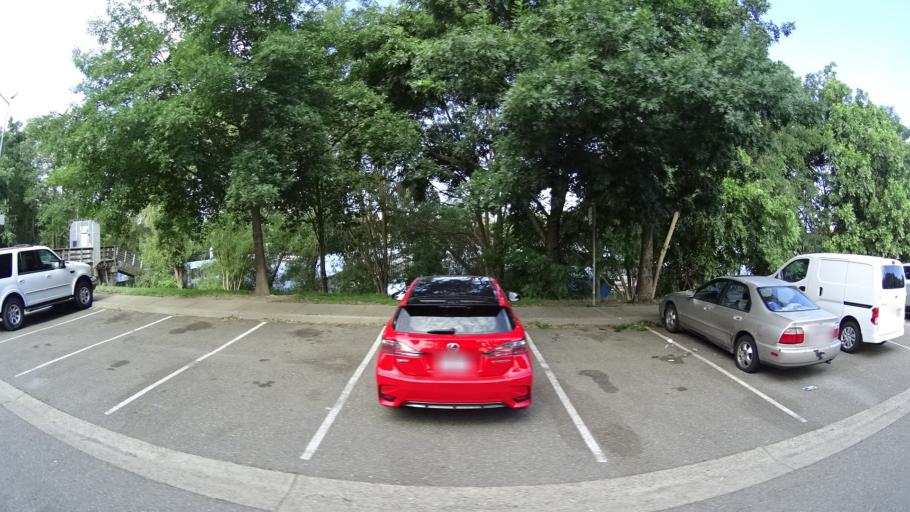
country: US
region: California
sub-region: Yolo County
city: West Sacramento
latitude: 38.5655
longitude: -121.5163
